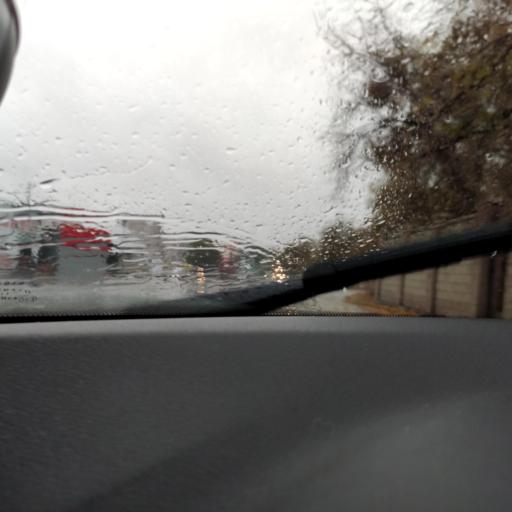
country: RU
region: Samara
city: Petra-Dubrava
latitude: 53.2431
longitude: 50.2725
